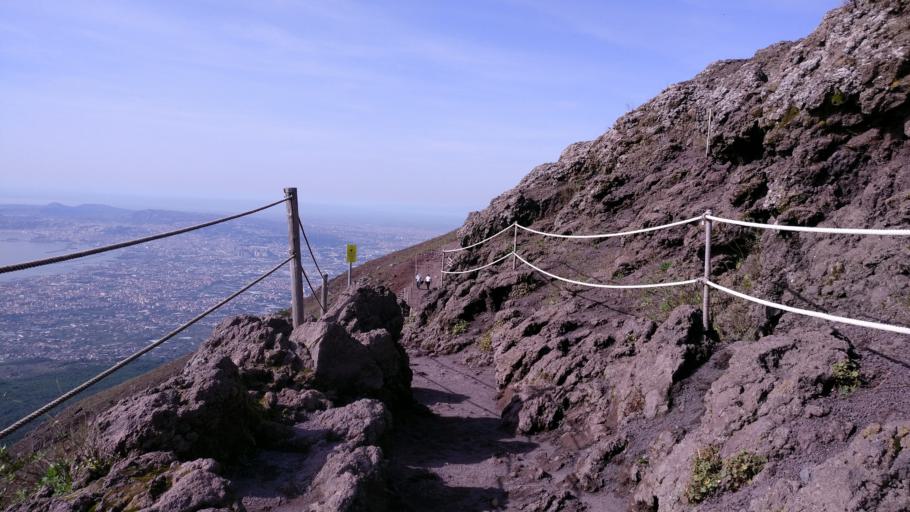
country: IT
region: Campania
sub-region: Provincia di Napoli
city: Torre del Greco
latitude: 40.8189
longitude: 14.4252
